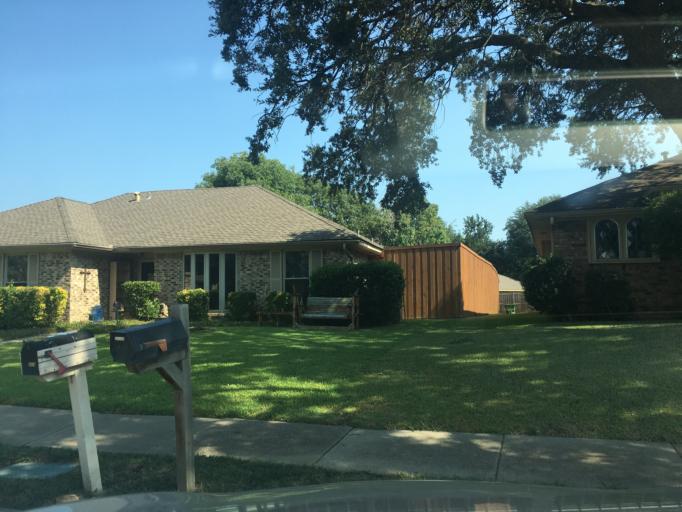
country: US
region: Texas
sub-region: Dallas County
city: Garland
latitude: 32.9412
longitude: -96.6365
